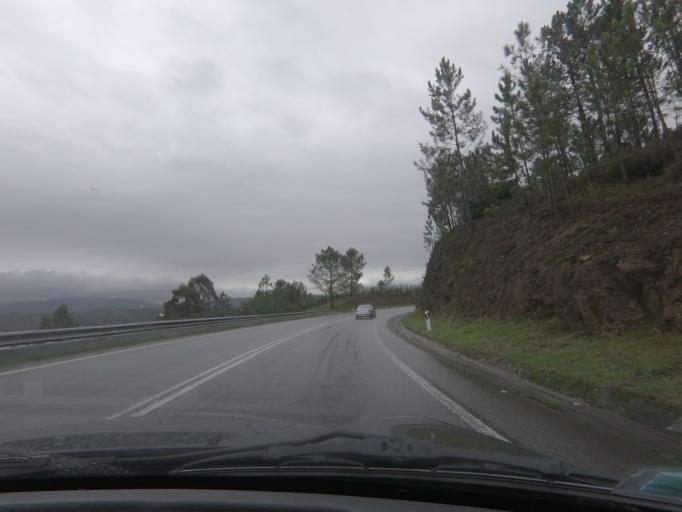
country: PT
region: Braga
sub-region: Celorico de Basto
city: Celorico de Basto
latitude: 41.3317
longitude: -8.0382
